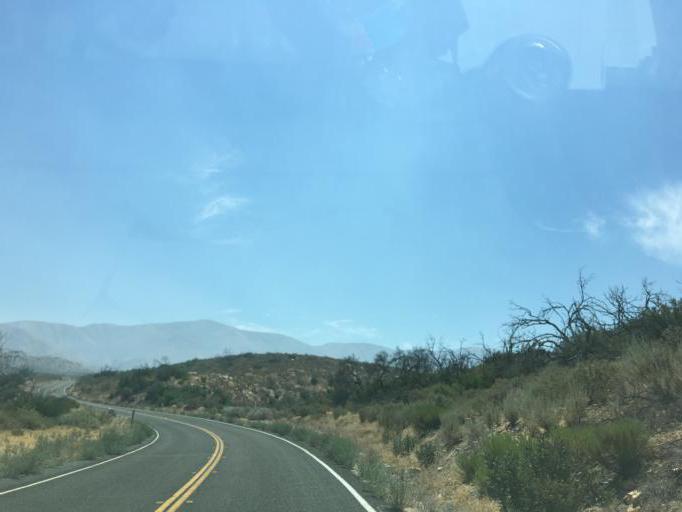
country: US
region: California
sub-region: Los Angeles County
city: Vincent
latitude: 34.4291
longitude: -118.1183
